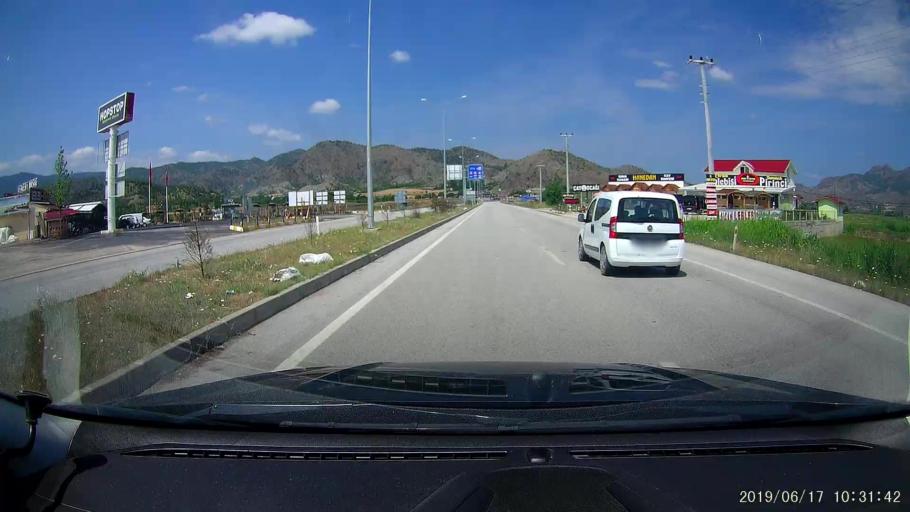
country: TR
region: Corum
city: Osmancik
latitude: 40.9783
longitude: 34.7824
